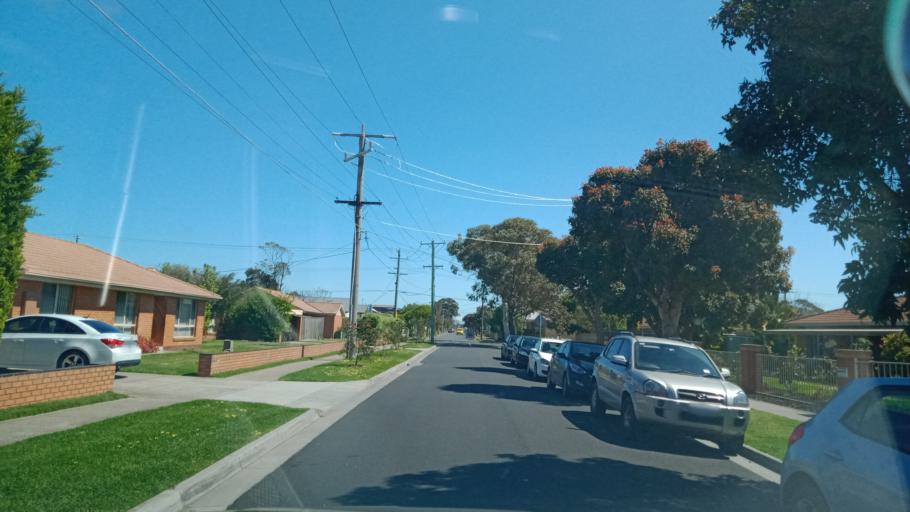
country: AU
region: Victoria
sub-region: Kingston
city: Chelsea
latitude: -38.0526
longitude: 145.1283
